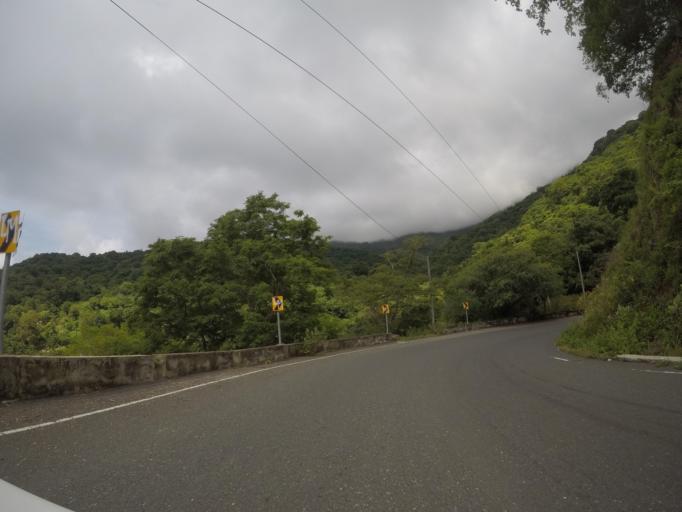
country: TL
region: Liquica
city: Maubara
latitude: -8.6773
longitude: 125.1096
